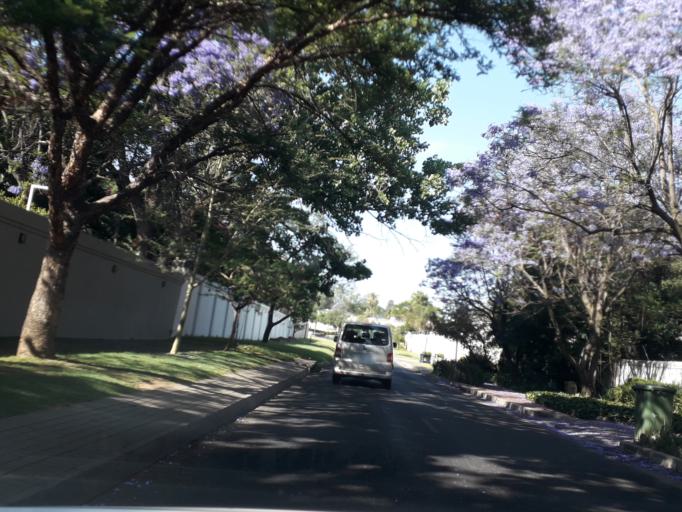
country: ZA
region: Gauteng
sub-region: City of Johannesburg Metropolitan Municipality
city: Midrand
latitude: -26.0447
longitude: 28.0325
